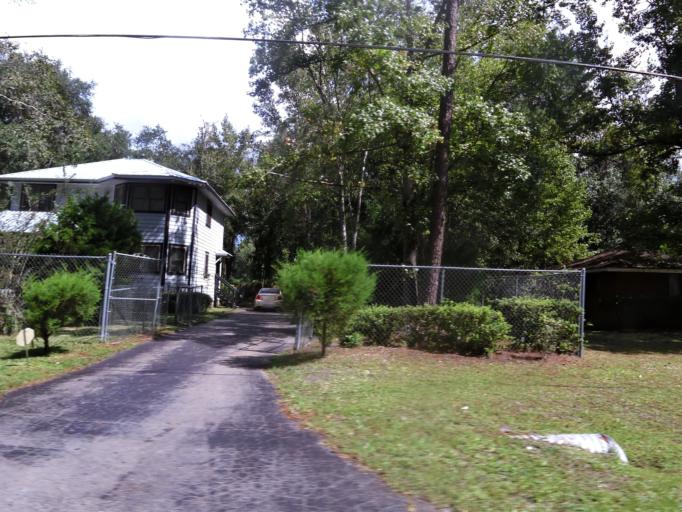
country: US
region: Florida
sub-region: Union County
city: Lake Butler
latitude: 30.0189
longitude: -82.3322
